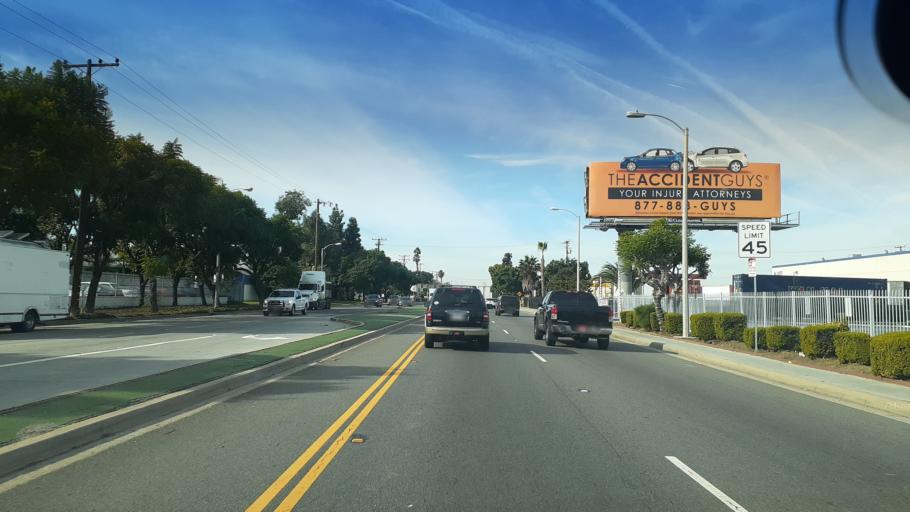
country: US
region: California
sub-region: Los Angeles County
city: Compton
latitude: 33.8467
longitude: -118.2123
